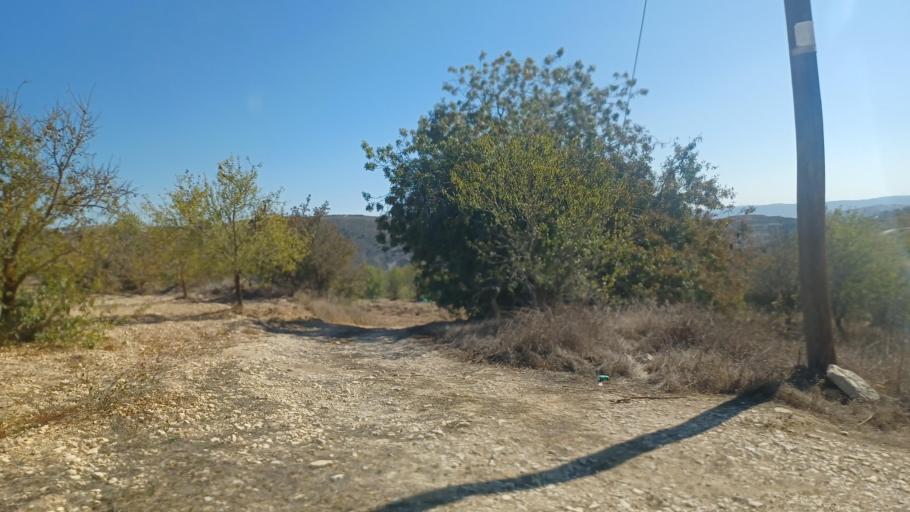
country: CY
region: Pafos
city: Mesogi
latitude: 34.8049
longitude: 32.4905
